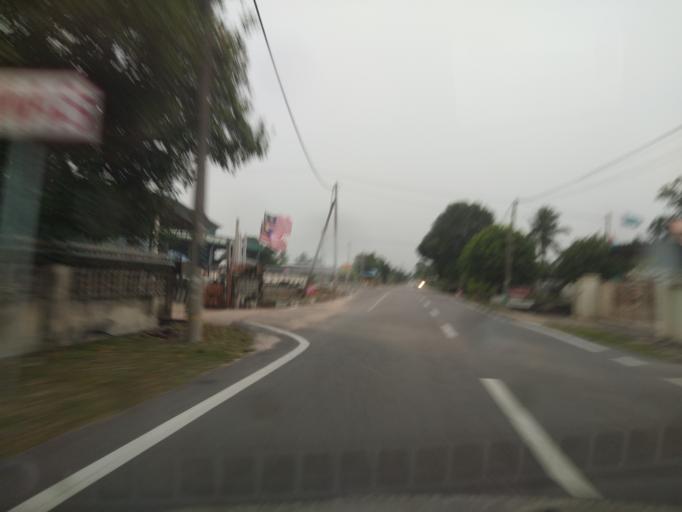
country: MY
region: Penang
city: Permatang Kuching
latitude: 5.4956
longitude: 100.3974
